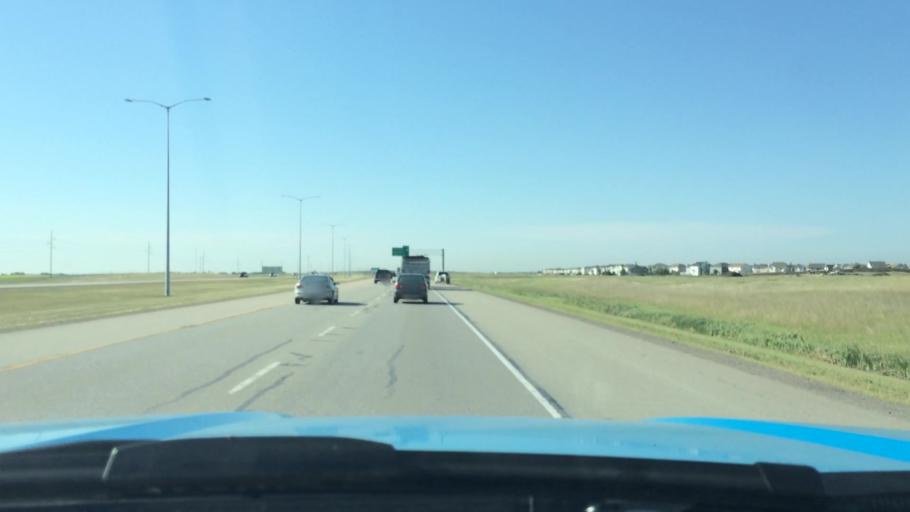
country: CA
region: Alberta
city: Chestermere
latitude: 51.1151
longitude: -113.9214
